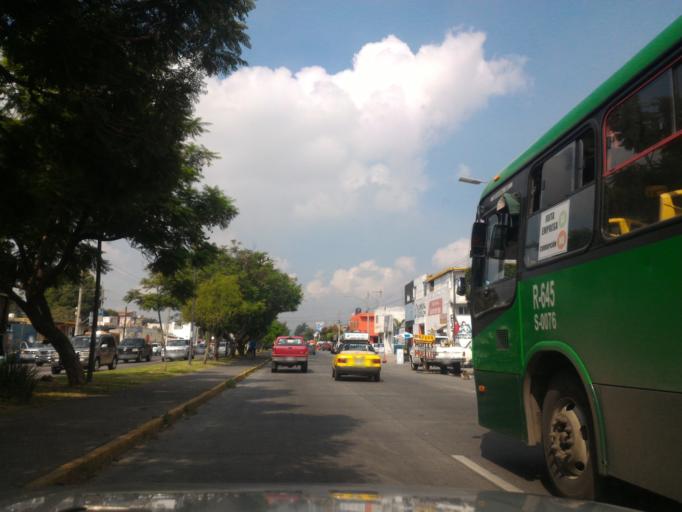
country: MX
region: Jalisco
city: Guadalajara
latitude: 20.6245
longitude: -103.3772
